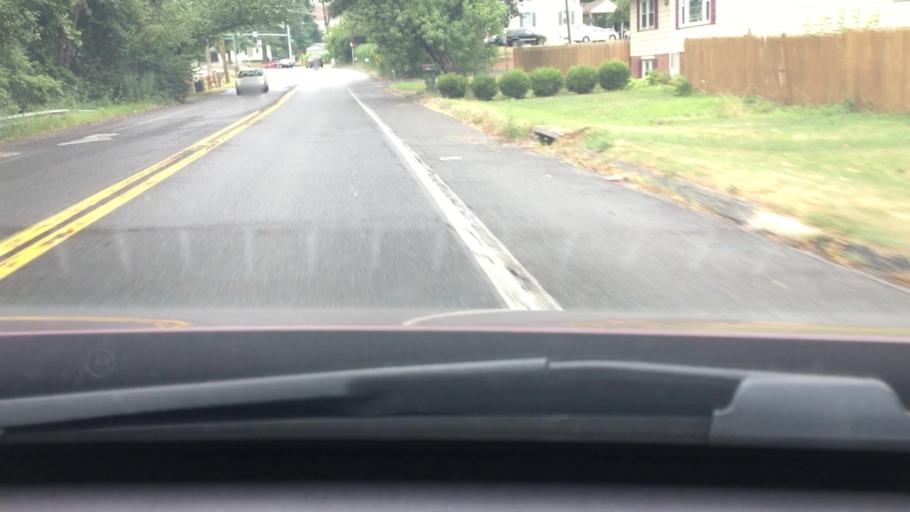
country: US
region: Maryland
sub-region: Prince George's County
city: Beltsville
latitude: 39.0394
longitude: -76.9119
